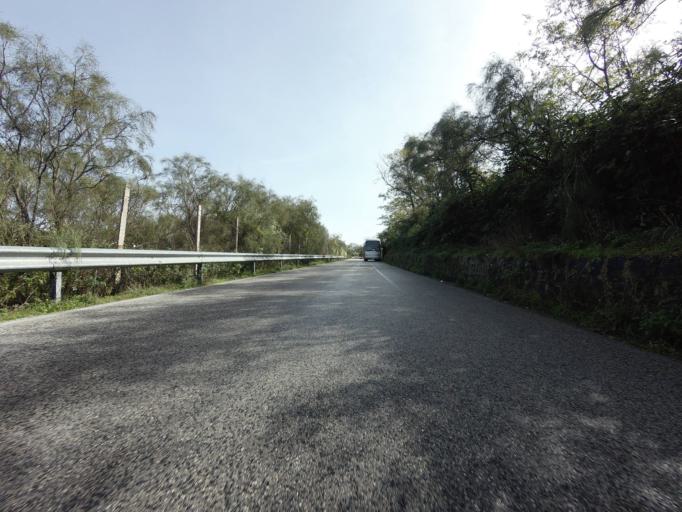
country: IT
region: Campania
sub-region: Provincia di Napoli
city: Somma Vesuviana
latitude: 40.8297
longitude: 14.4293
